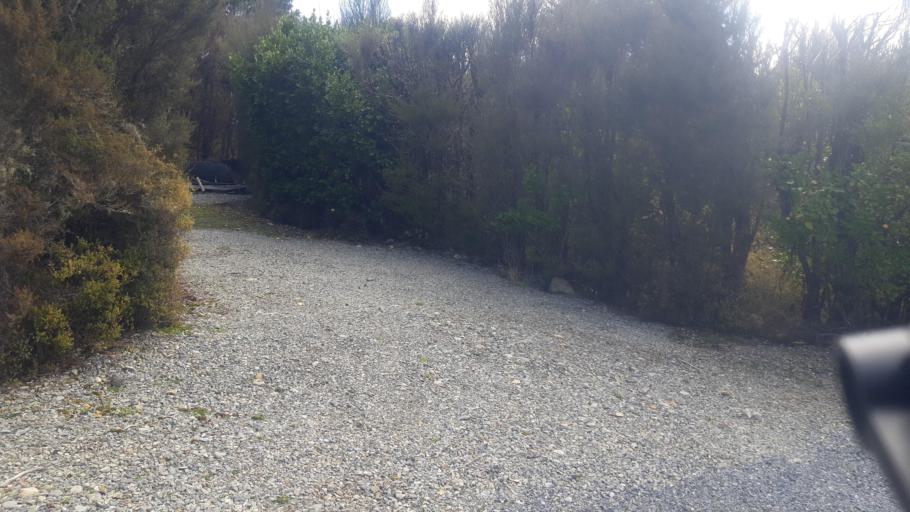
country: NZ
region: Tasman
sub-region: Tasman District
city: Wakefield
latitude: -41.8061
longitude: 172.8403
